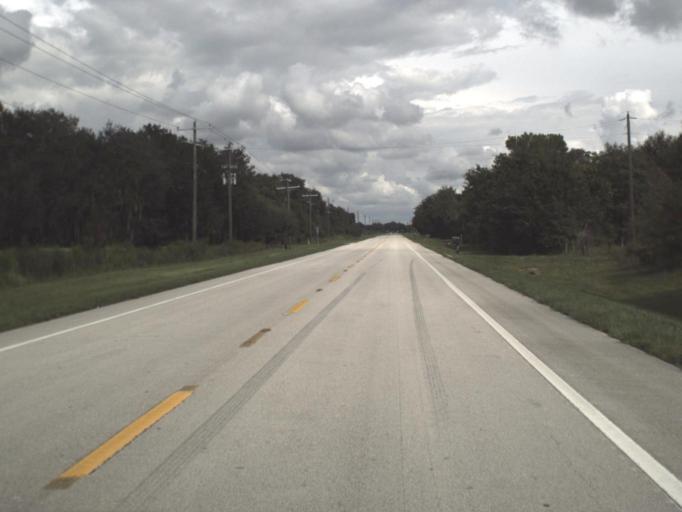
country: US
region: Florida
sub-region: DeSoto County
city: Nocatee
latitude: 27.2009
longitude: -81.9737
